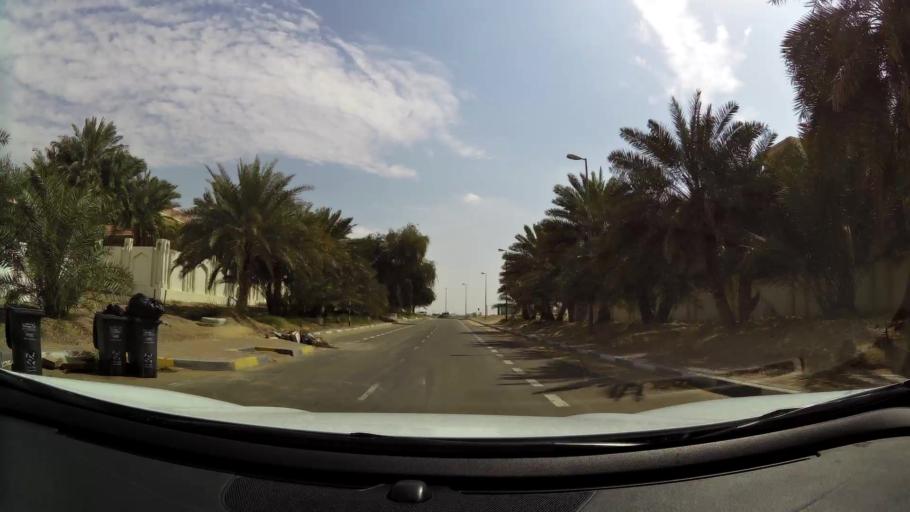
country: AE
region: Abu Dhabi
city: Al Ain
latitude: 24.1888
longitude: 55.7943
